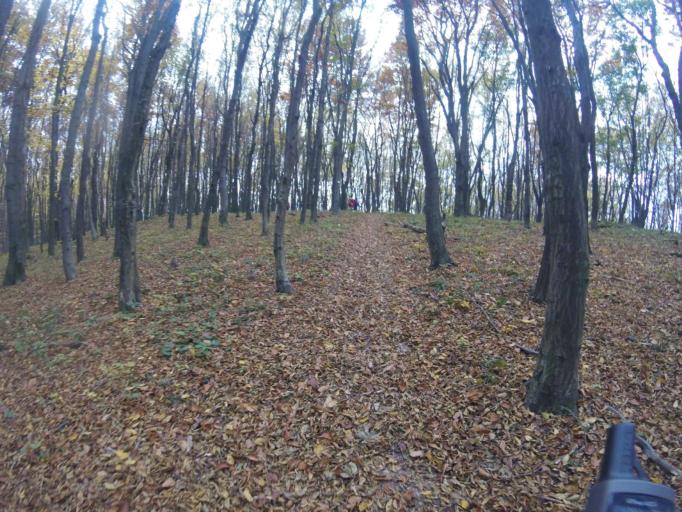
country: HU
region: Borsod-Abauj-Zemplen
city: Gonc
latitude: 48.4382
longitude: 21.3189
